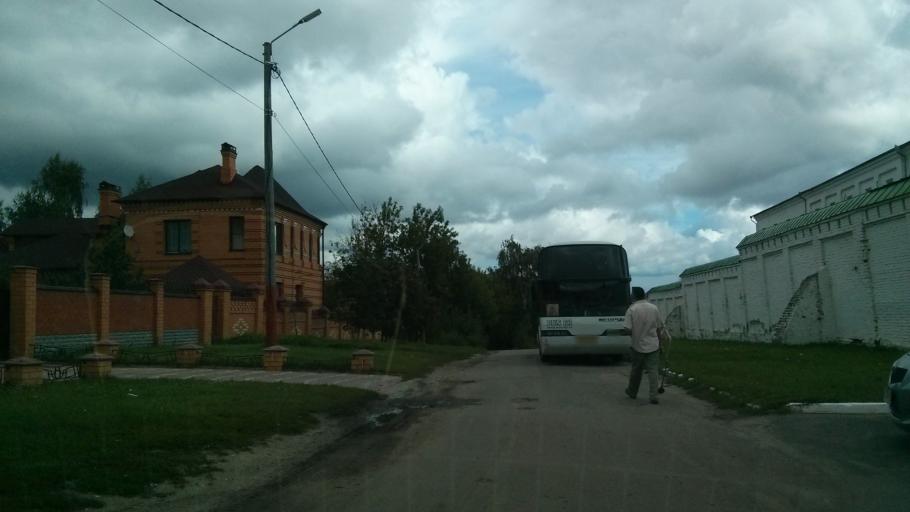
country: RU
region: Vladimir
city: Murom
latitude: 55.5734
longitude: 42.0652
